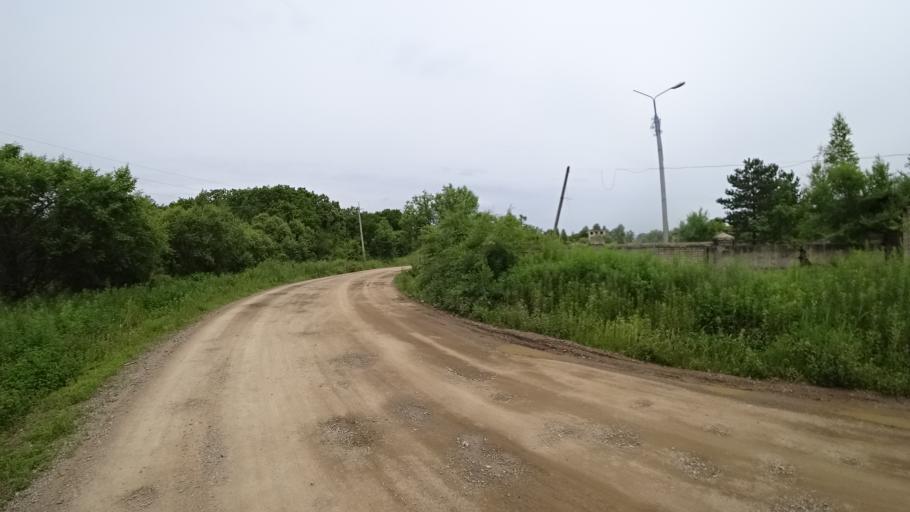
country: RU
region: Primorskiy
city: Arsen'yev
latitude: 44.1972
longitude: 133.3074
